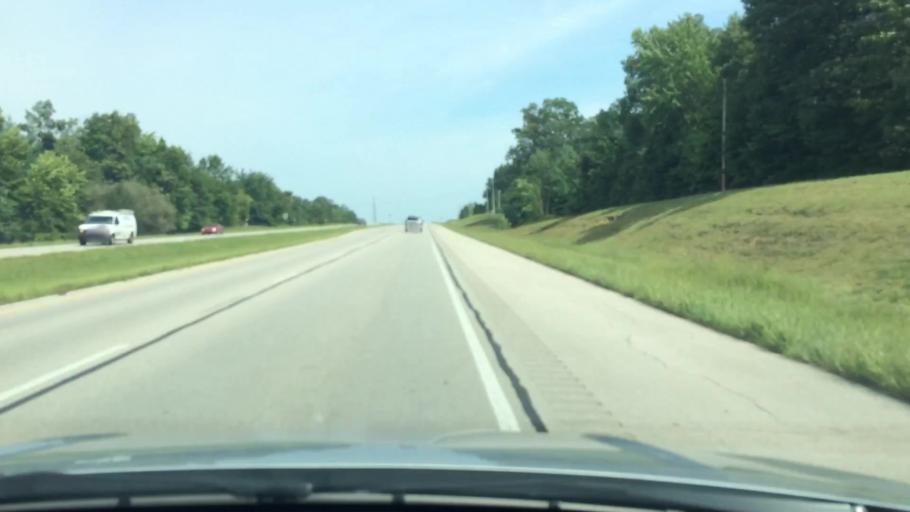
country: US
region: Kentucky
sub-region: Anderson County
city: Lawrenceburg
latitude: 38.0809
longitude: -84.9177
